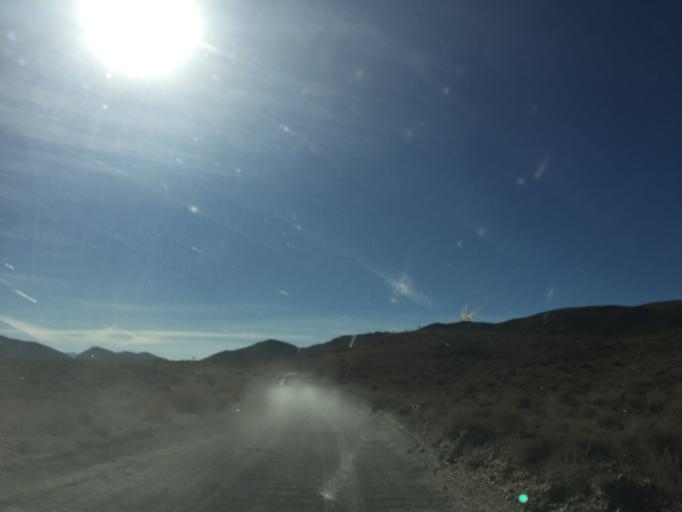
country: US
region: California
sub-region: Inyo County
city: Lone Pine
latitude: 36.8371
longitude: -117.5038
